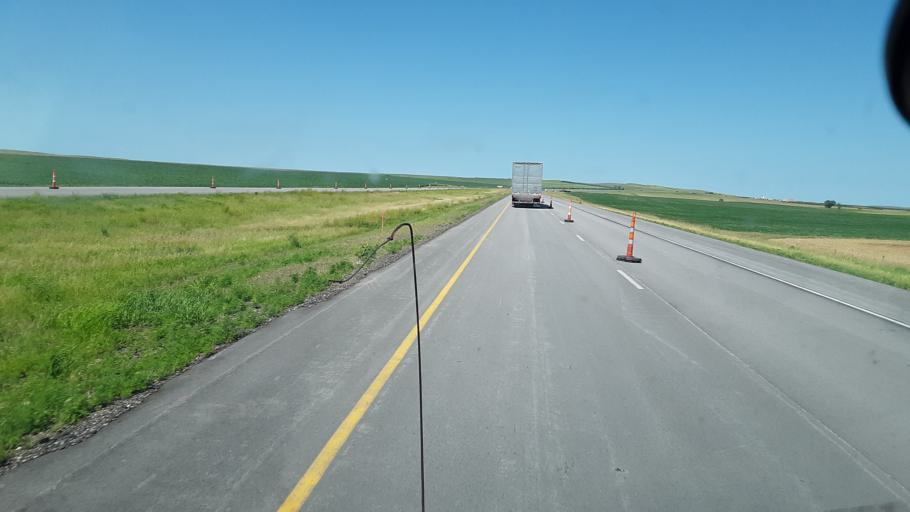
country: US
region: South Dakota
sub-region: Lyman County
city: Kennebec
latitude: 43.8986
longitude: -100.1292
